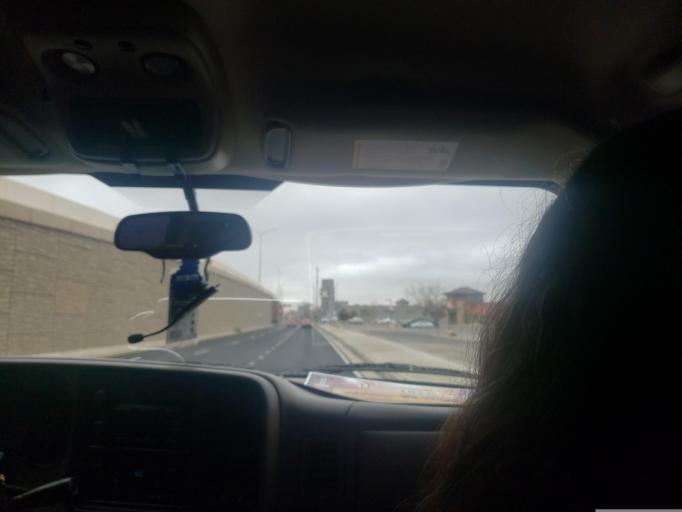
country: US
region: New Mexico
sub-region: Bernalillo County
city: Albuquerque
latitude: 35.1111
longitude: -106.7023
